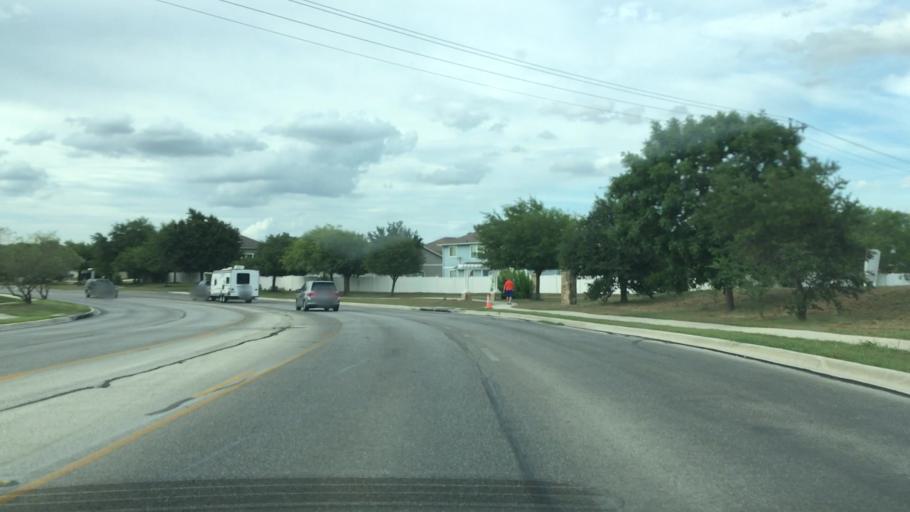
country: US
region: Texas
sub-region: Guadalupe County
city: Cibolo
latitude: 29.5898
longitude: -98.2492
